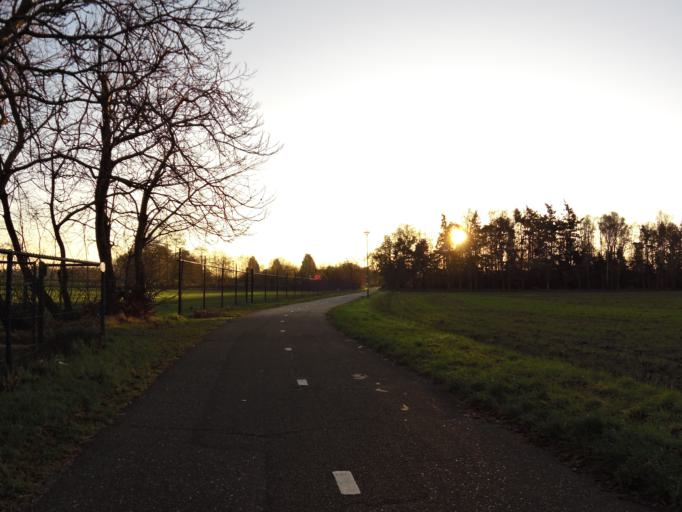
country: NL
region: North Brabant
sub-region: Gemeente Sint-Michielsgestel
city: Sint-Michielsgestel
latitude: 51.6460
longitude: 5.3341
